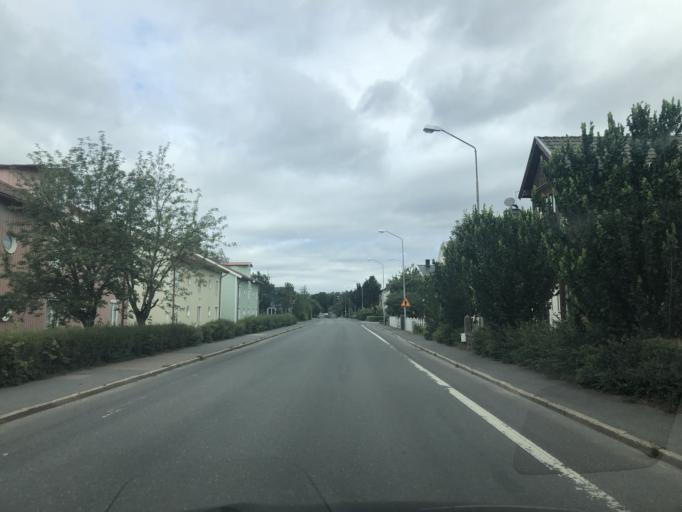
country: SE
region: Joenkoeping
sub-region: Vaggeryds Kommun
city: Vaggeryd
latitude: 57.5004
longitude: 14.1470
